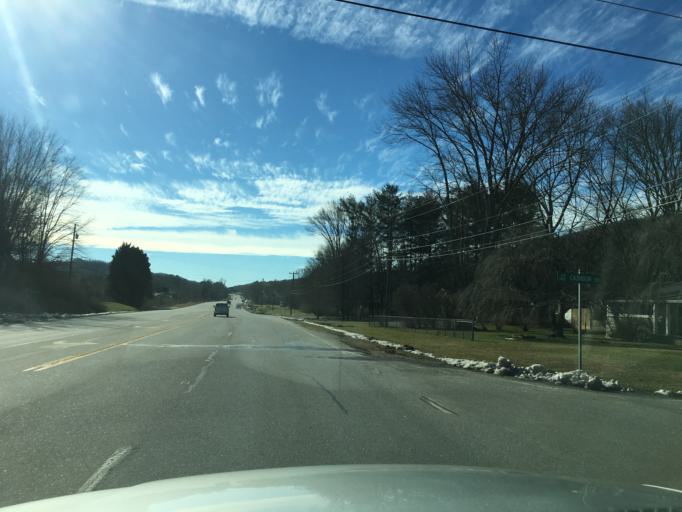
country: US
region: North Carolina
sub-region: Henderson County
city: Etowah
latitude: 35.3443
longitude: -82.6250
